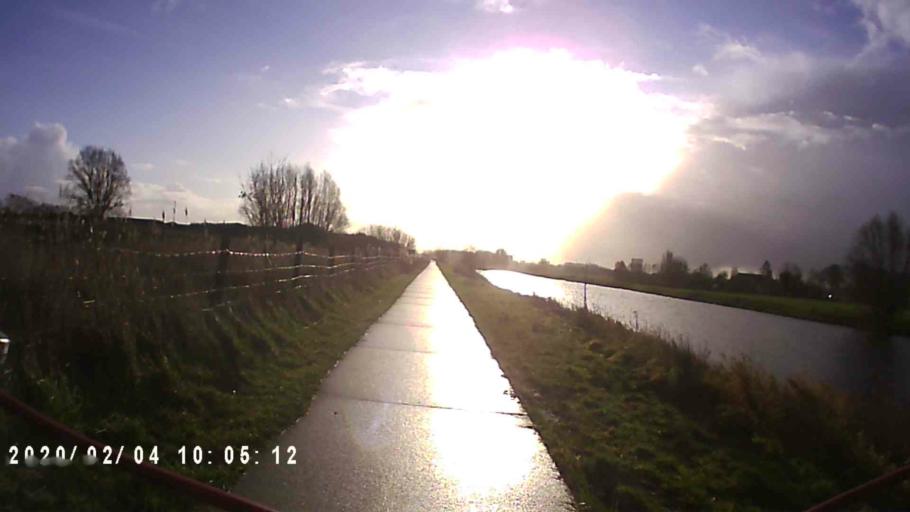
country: NL
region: Groningen
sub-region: Gemeente Zuidhorn
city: Aduard
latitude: 53.2540
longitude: 6.5126
